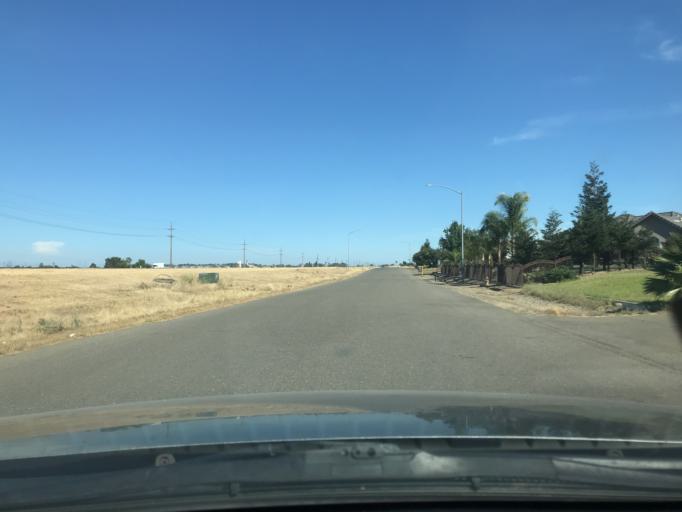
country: US
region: California
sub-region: Merced County
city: Merced
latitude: 37.3382
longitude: -120.5393
